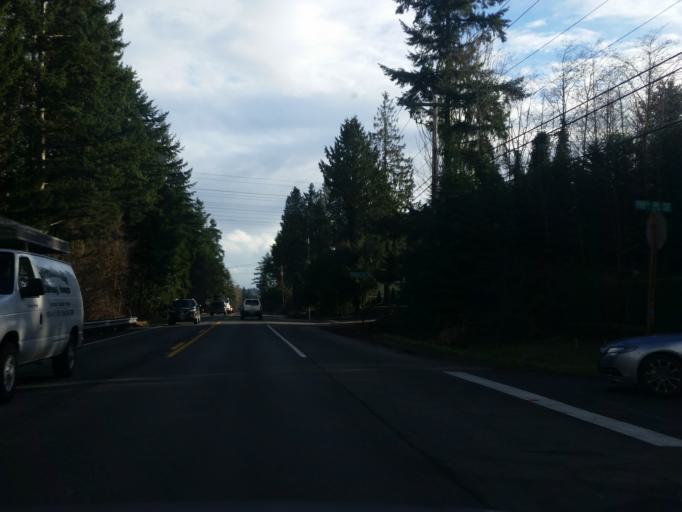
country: US
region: Washington
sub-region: Snohomish County
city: Martha Lake
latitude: 47.8179
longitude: -122.2309
